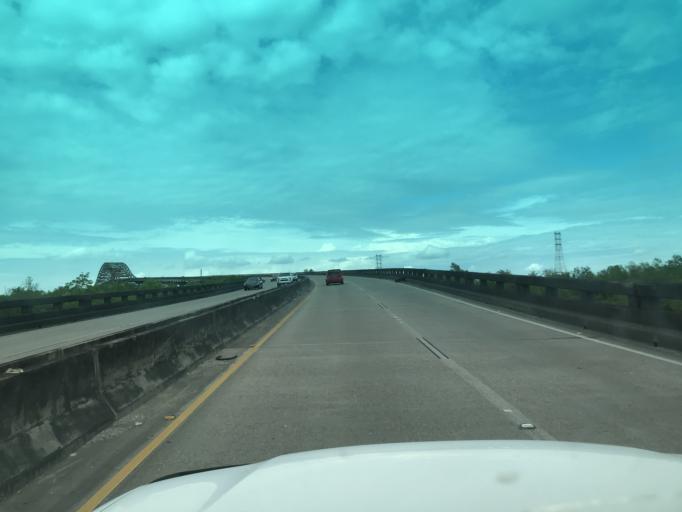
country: US
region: Louisiana
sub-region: Saint Bernard Parish
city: Chalmette
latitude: 29.9968
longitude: -89.9395
